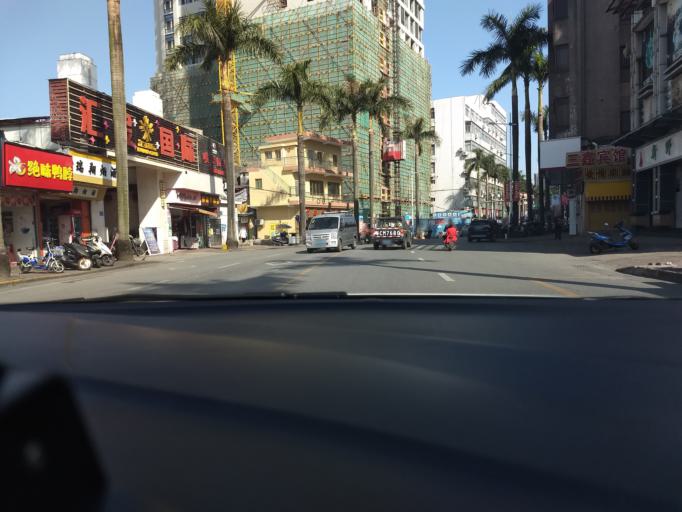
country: CN
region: Guangdong
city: Dagang
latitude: 22.8068
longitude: 113.4034
